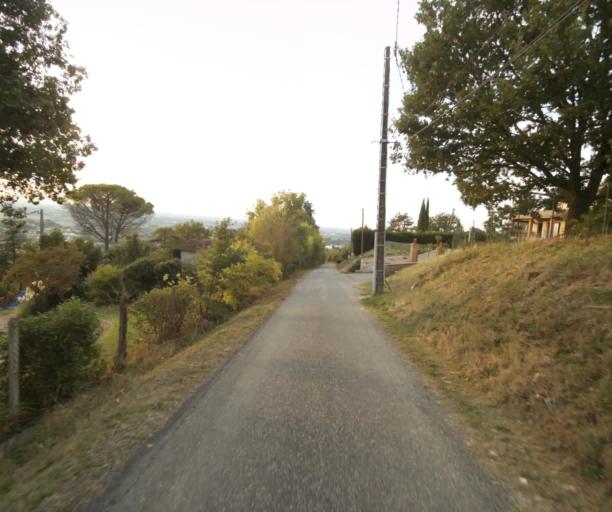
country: FR
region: Midi-Pyrenees
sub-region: Departement du Tarn-et-Garonne
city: Pompignan
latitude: 43.8290
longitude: 1.3099
